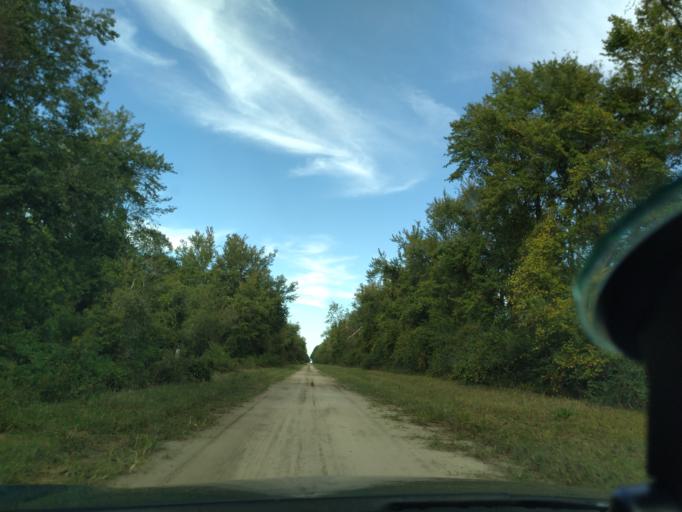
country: US
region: North Carolina
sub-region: Beaufort County
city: Belhaven
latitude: 35.7180
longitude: -76.5810
